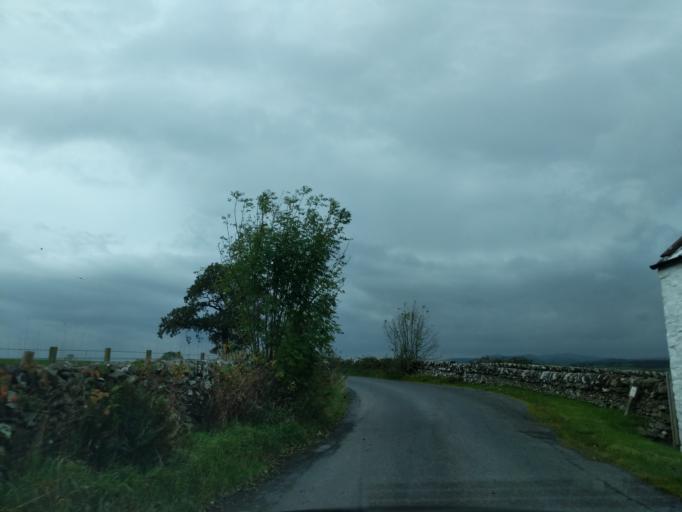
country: GB
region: Scotland
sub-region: Dumfries and Galloway
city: Castle Douglas
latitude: 54.9254
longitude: -3.9517
